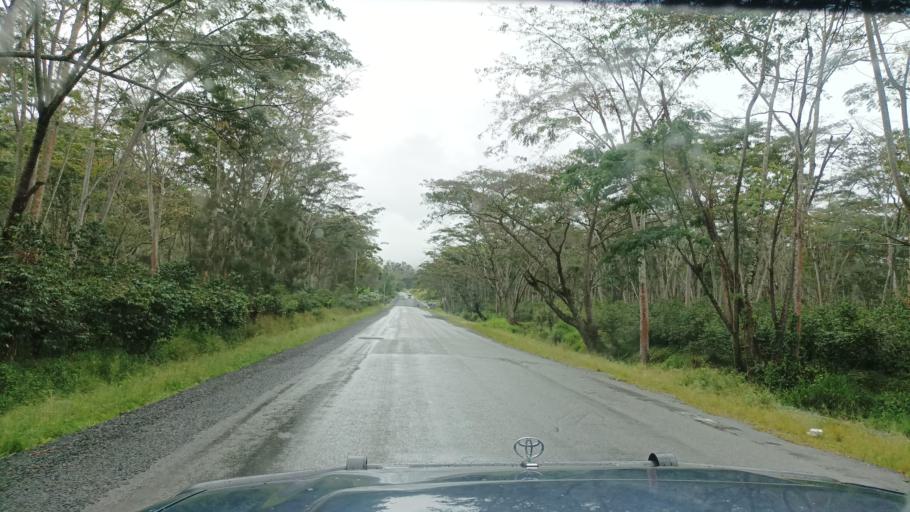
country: PG
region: Western Highlands
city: Rauna
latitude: -5.8332
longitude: 144.3511
